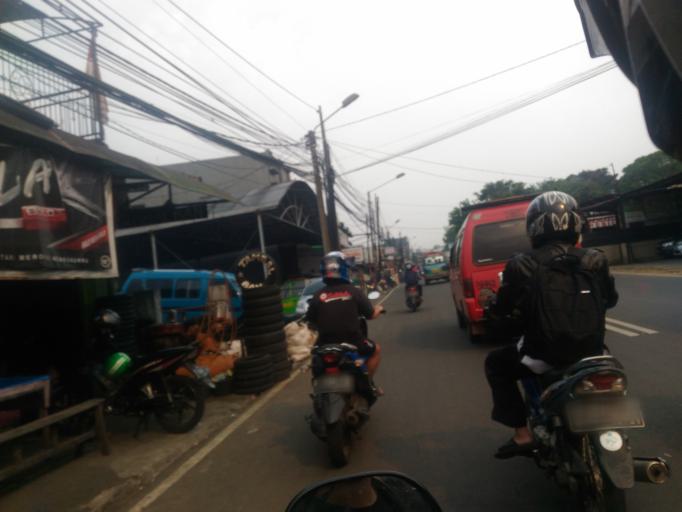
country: ID
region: West Java
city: Bogor
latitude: -6.6386
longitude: 106.8325
